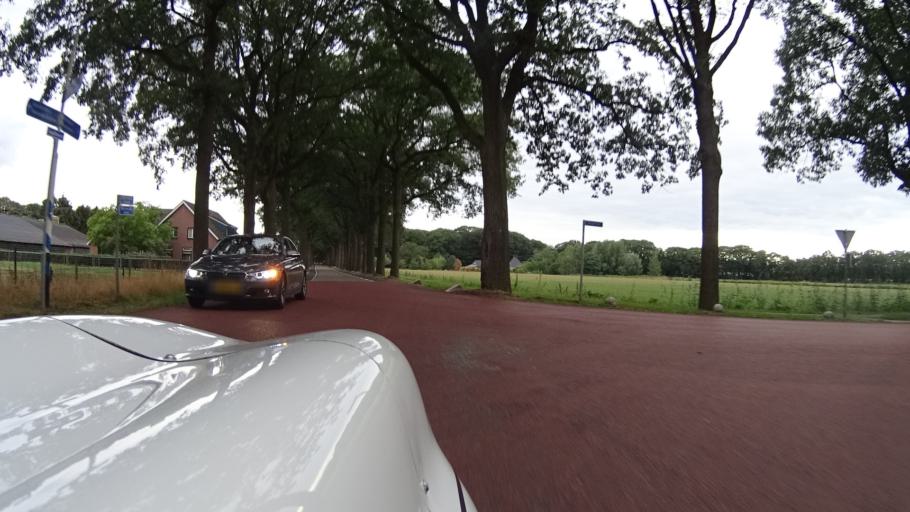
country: NL
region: North Brabant
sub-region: Gemeente Maasdonk
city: Geffen
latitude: 51.6953
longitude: 5.4534
